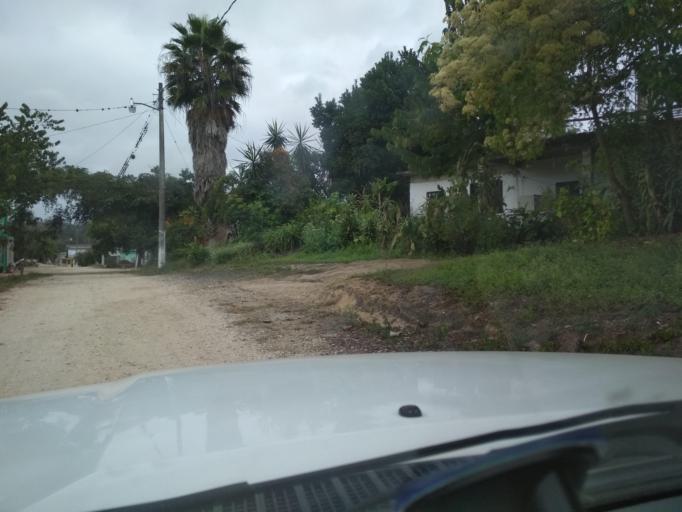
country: MX
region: Veracruz
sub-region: Emiliano Zapata
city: Dos Rios
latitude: 19.5371
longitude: -96.7951
